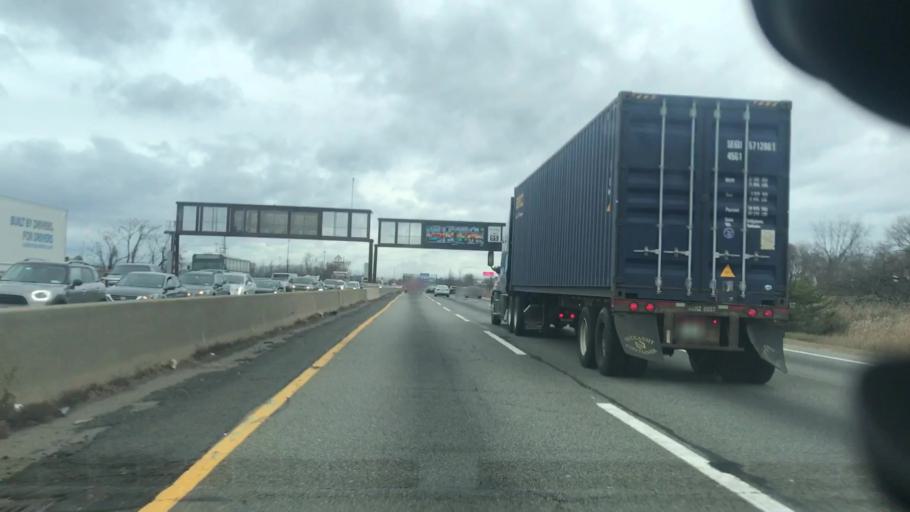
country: US
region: New Jersey
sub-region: Hudson County
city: North Bergen
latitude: 40.8178
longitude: -74.0280
